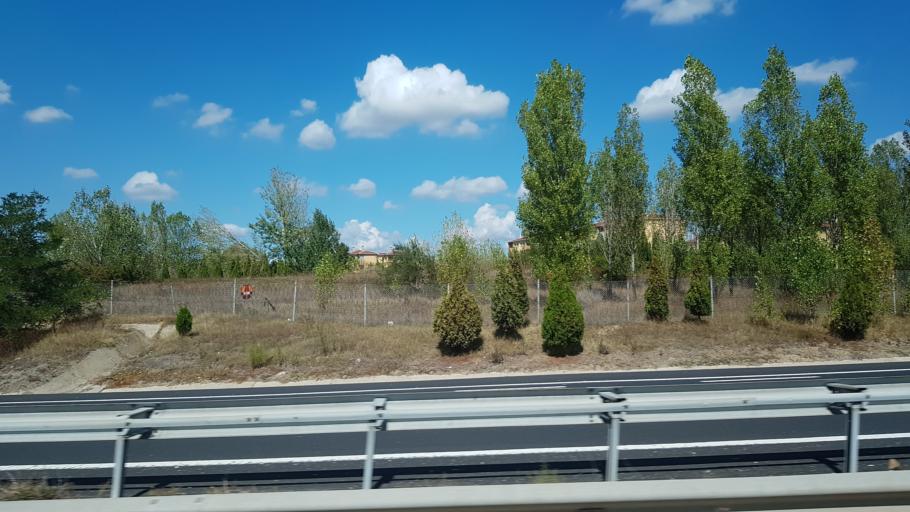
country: TR
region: Tekirdag
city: Velimese
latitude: 41.2213
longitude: 27.8666
